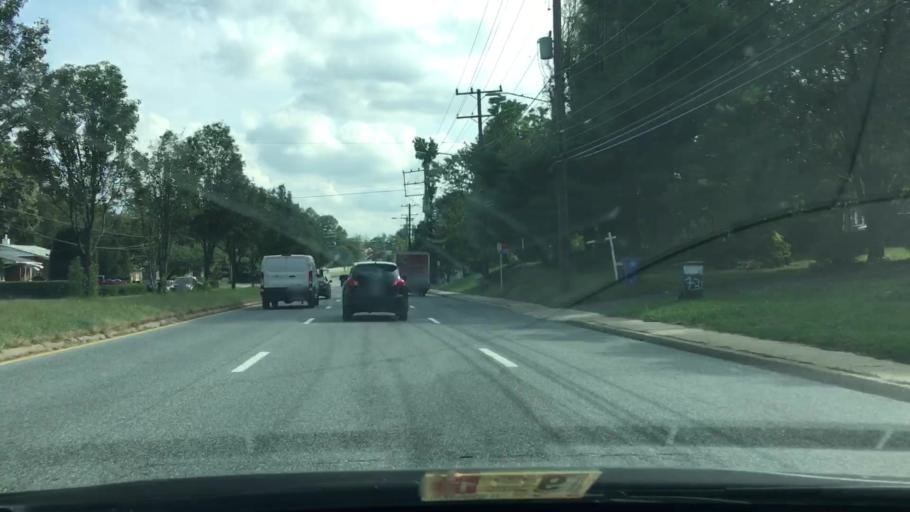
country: US
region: Maryland
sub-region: Montgomery County
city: Kemp Mill
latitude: 39.0314
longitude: -77.0224
